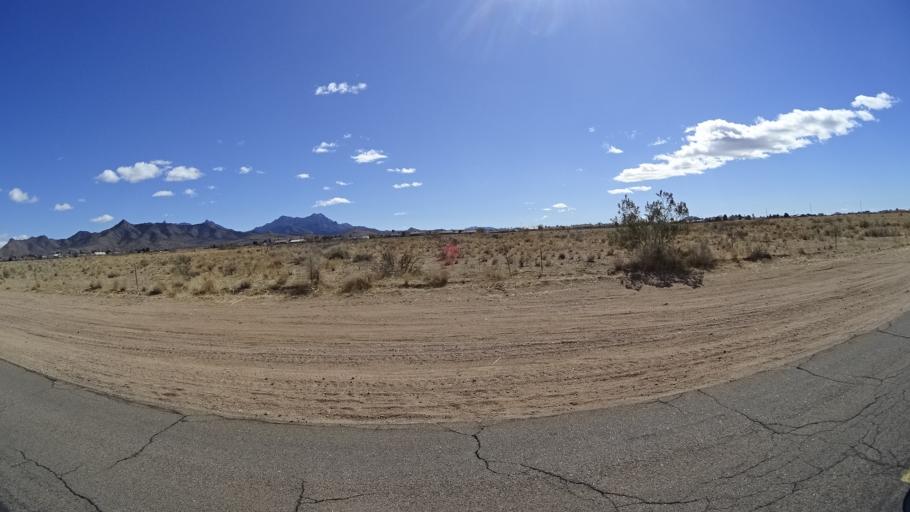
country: US
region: Arizona
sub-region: Mohave County
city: Kingman
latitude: 35.2019
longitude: -113.9825
